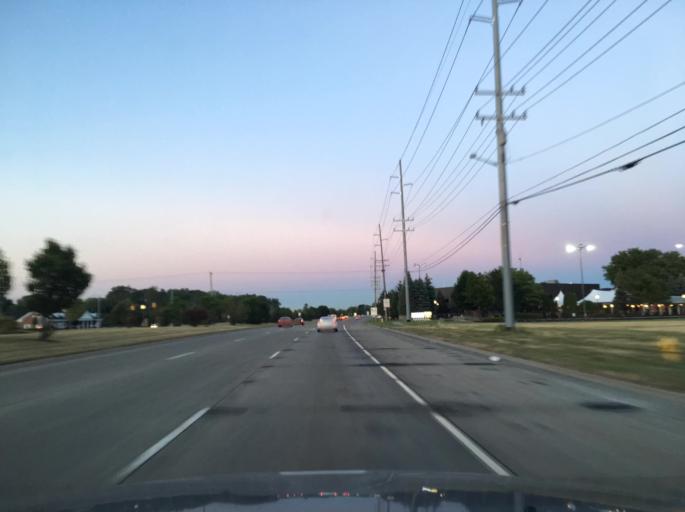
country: US
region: Michigan
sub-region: Macomb County
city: Mount Clemens
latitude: 42.6286
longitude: -82.8977
